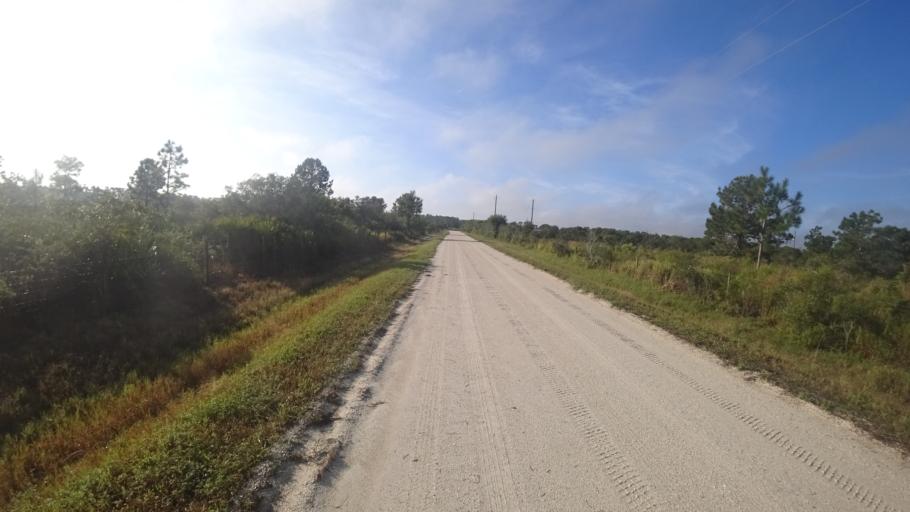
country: US
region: Florida
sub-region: Sarasota County
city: Fruitville
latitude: 27.4032
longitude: -82.2875
